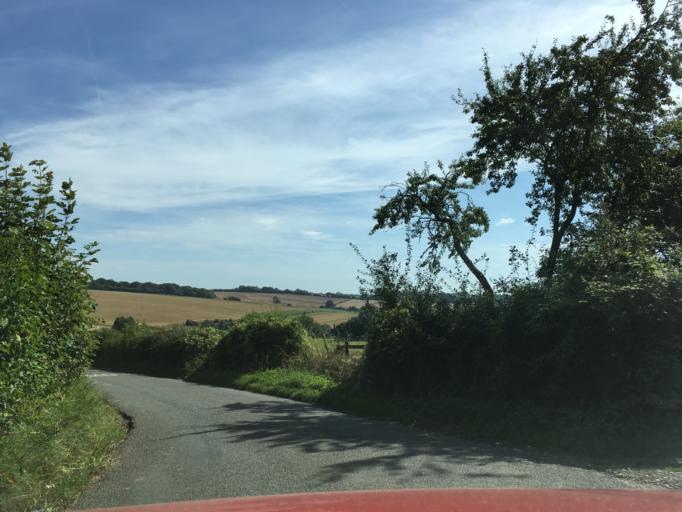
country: GB
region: England
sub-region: Hampshire
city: Highclere
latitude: 51.2895
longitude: -1.3704
